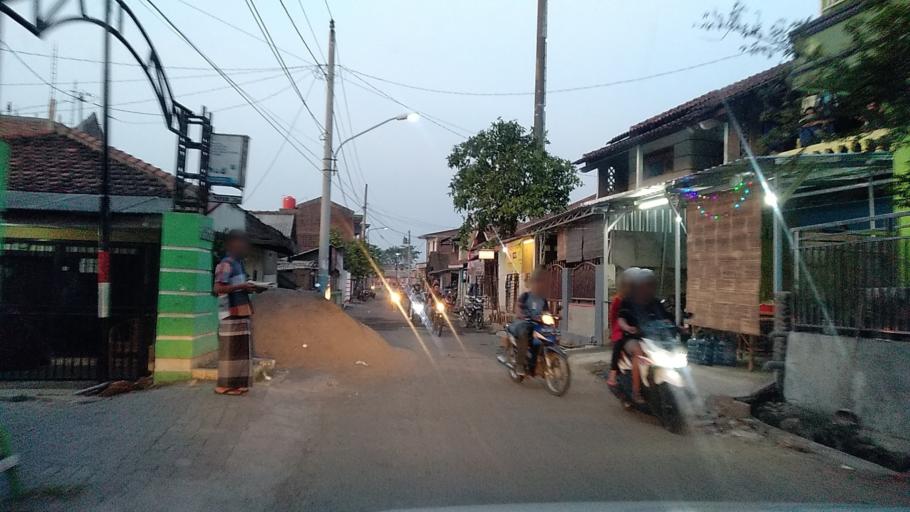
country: ID
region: Central Java
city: Semarang
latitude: -6.9730
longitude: 110.3334
